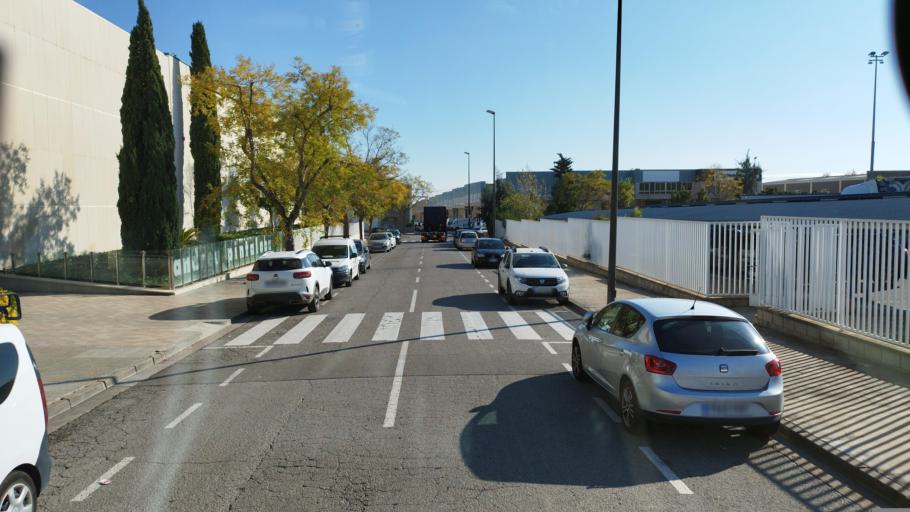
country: ES
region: Catalonia
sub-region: Provincia de Tarragona
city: Reus
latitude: 41.1576
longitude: 1.0768
